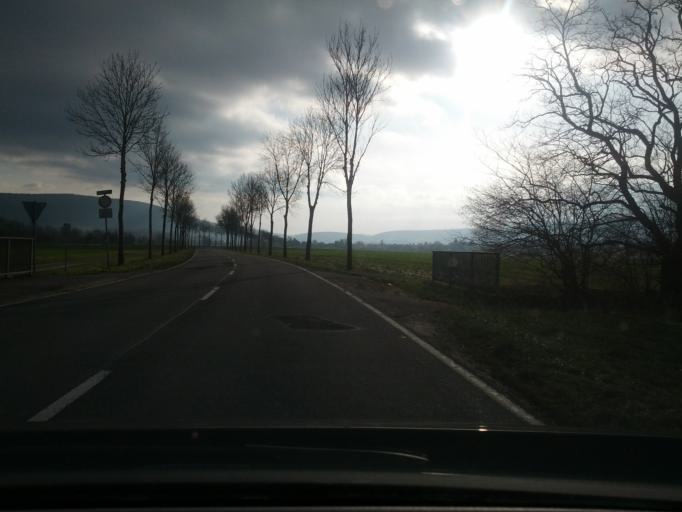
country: DE
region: Lower Saxony
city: Buhren
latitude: 51.5108
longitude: 9.5910
